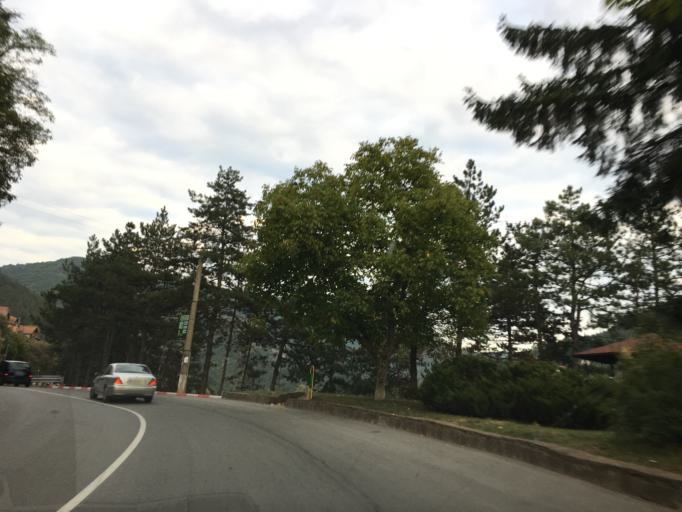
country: BG
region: Sofiya
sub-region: Obshtina Svoge
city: Svoge
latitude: 42.9536
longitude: 23.3637
